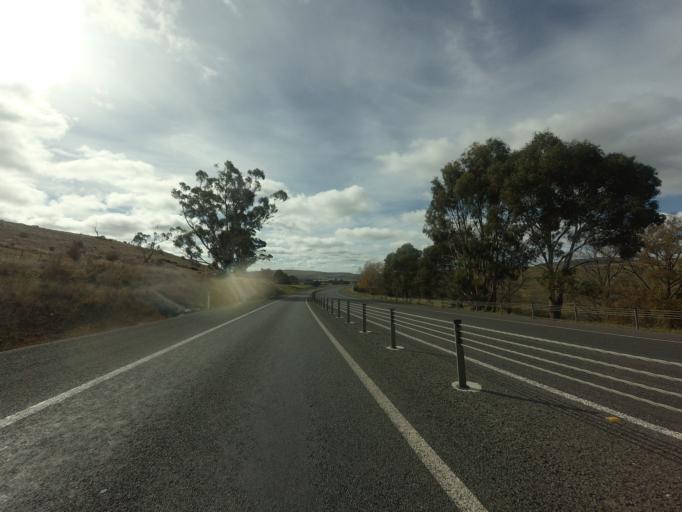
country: AU
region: Tasmania
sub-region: Brighton
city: Bridgewater
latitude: -42.3919
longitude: 147.2778
